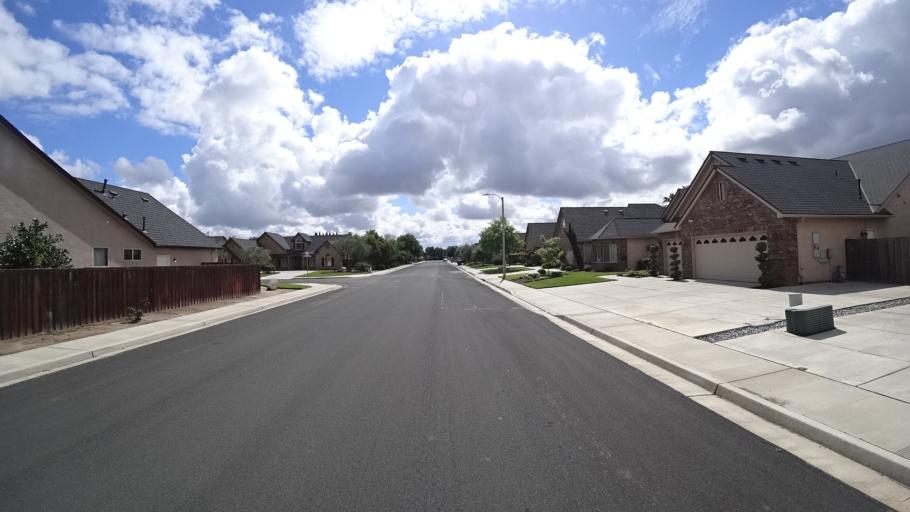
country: US
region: California
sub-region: Kings County
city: Lucerne
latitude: 36.3705
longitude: -119.6535
